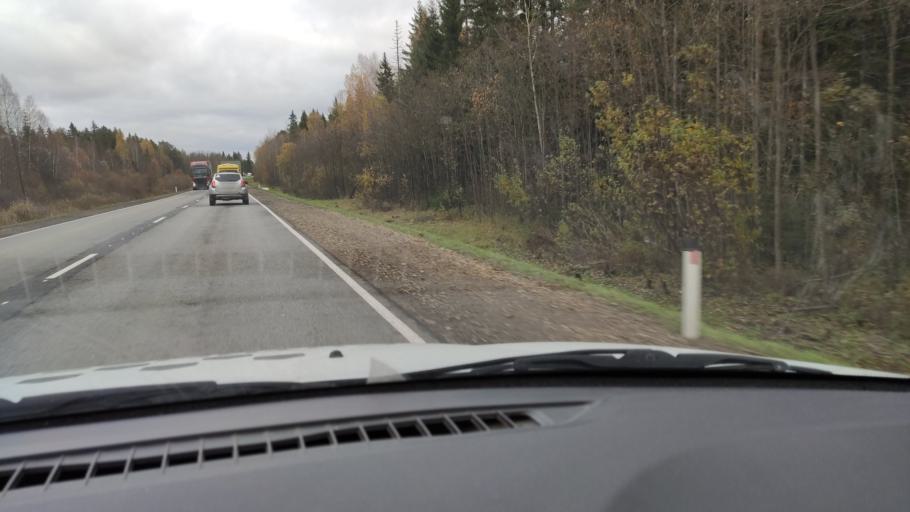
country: RU
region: Kirov
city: Slobodskoy
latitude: 58.7800
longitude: 50.4066
